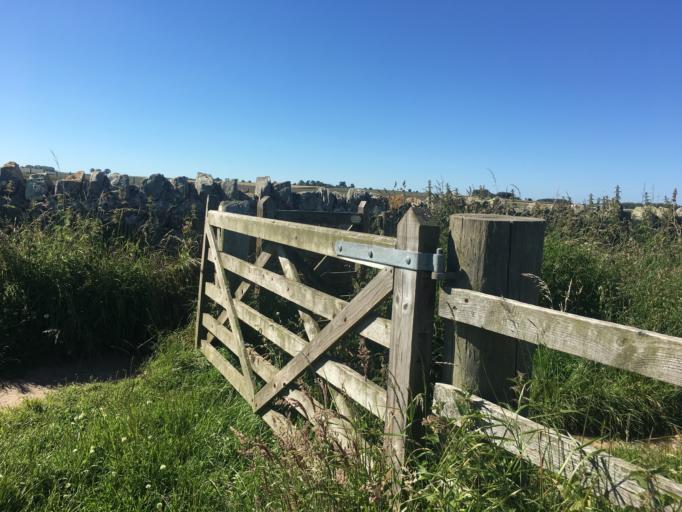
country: GB
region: England
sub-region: Northumberland
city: Beadnell
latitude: 55.5446
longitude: -1.6392
